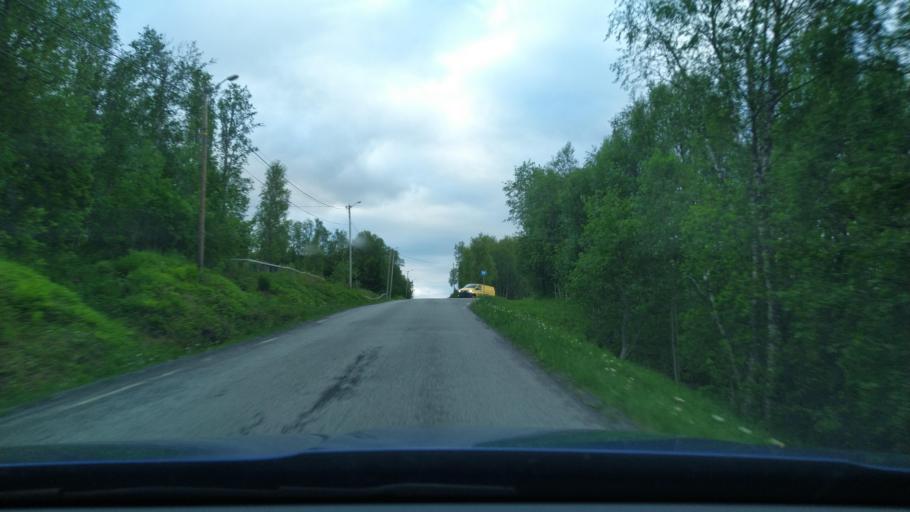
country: NO
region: Troms
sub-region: Tranoy
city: Vangsvika
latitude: 69.1289
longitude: 17.8635
